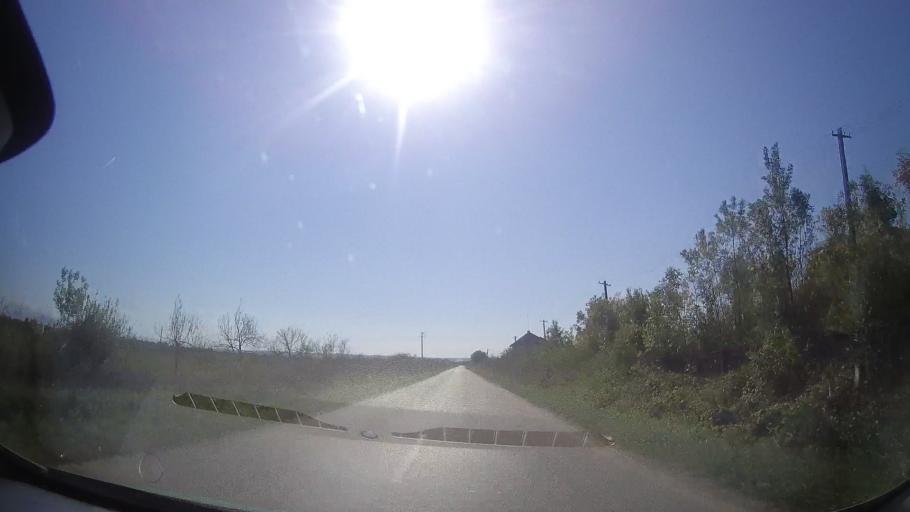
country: RO
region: Timis
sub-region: Comuna Bethausen
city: Bethausen
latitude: 45.8271
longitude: 21.9596
